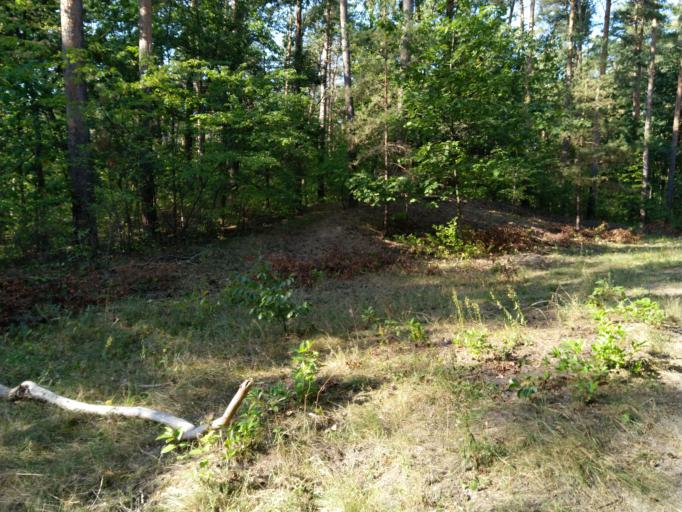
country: DE
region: Brandenburg
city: Woltersdorf
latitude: 52.4483
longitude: 13.7297
